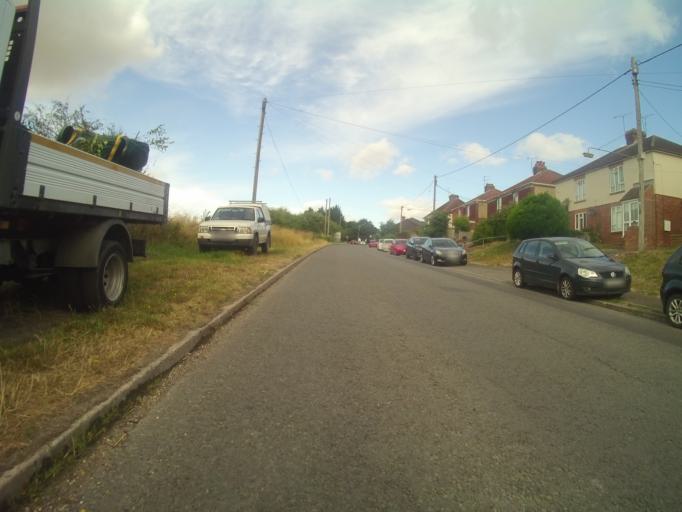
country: GB
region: England
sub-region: Wiltshire
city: Durrington
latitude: 51.1953
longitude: -1.7804
